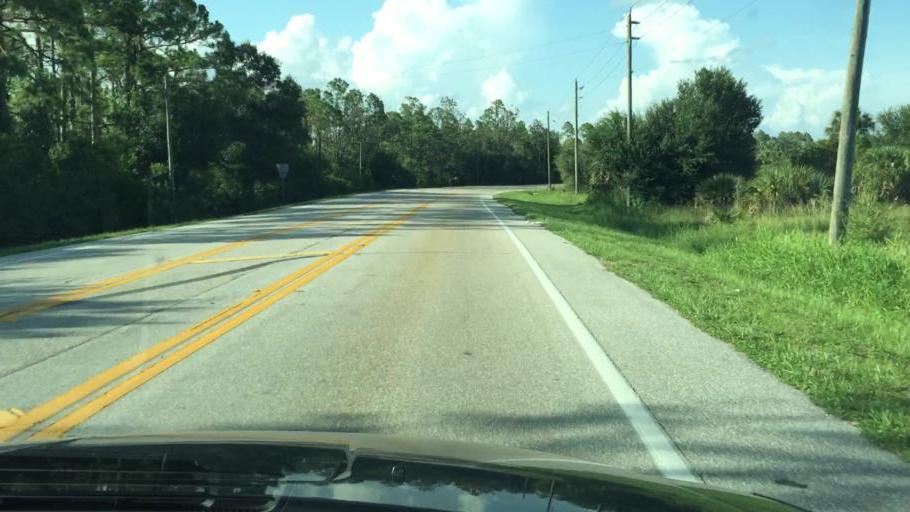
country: US
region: Florida
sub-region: Lee County
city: Buckingham
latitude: 26.6328
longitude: -81.7557
